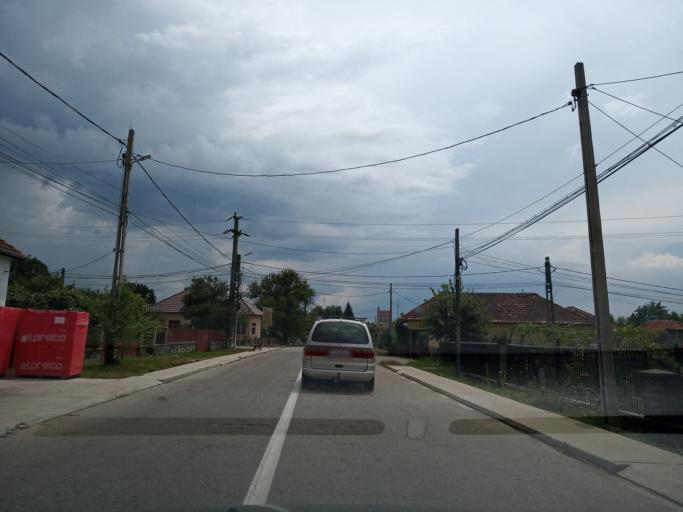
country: RO
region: Gorj
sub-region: Comuna Tismana
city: Tismana
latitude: 45.0571
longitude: 22.9456
